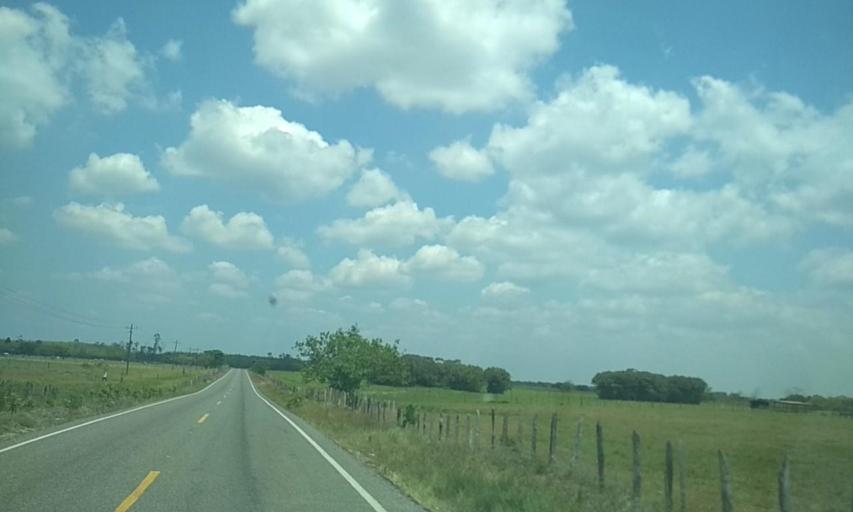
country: MX
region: Tabasco
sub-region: Huimanguillo
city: Huapacal 1ra. Seccion
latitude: 17.7530
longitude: -93.7186
